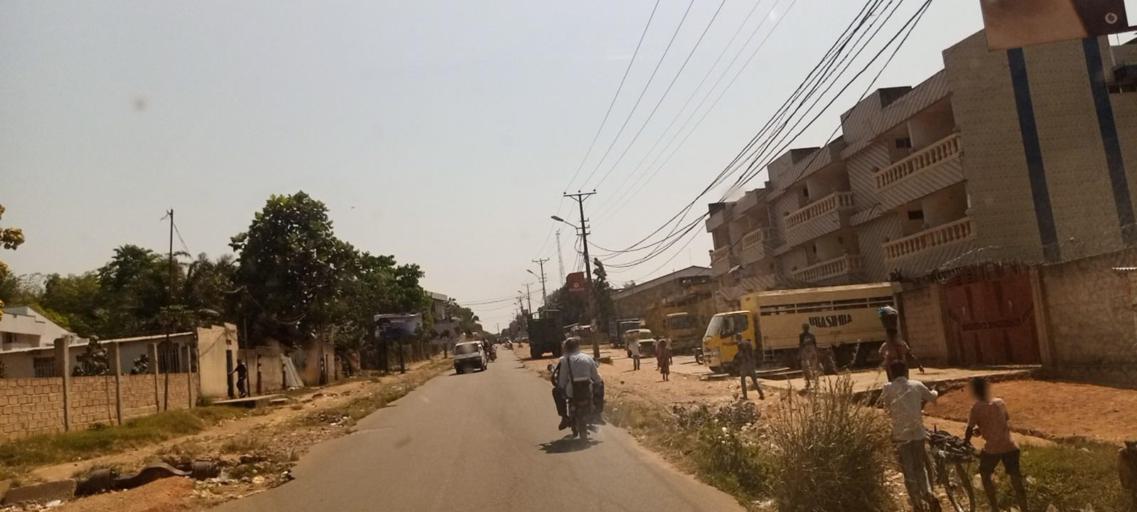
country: CD
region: Kasai-Oriental
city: Mbuji-Mayi
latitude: -6.1225
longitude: 23.5952
